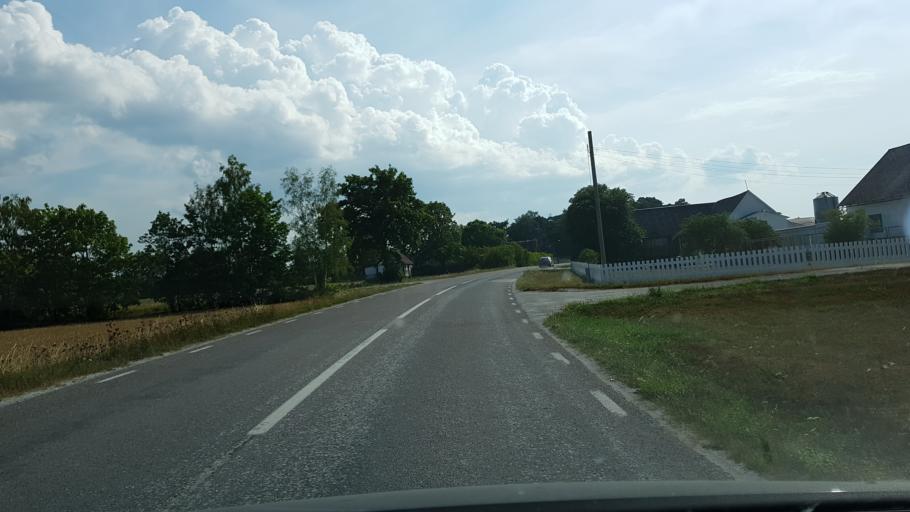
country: SE
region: Gotland
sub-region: Gotland
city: Visby
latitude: 57.8051
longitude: 18.5236
